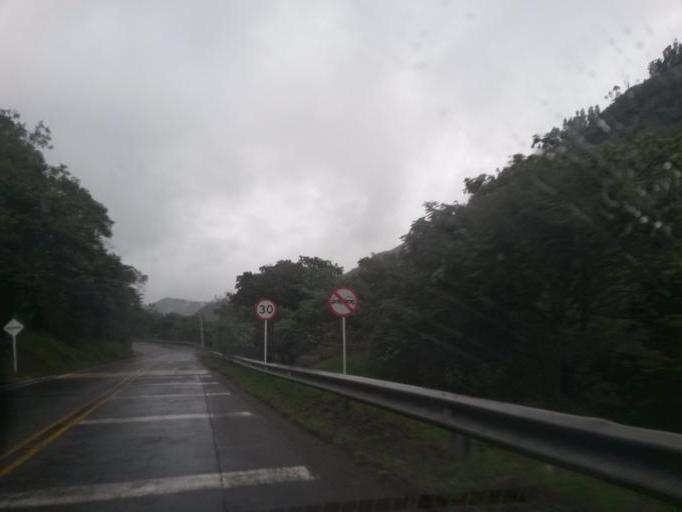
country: CO
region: Cauca
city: Popayan
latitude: 2.3969
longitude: -76.4992
